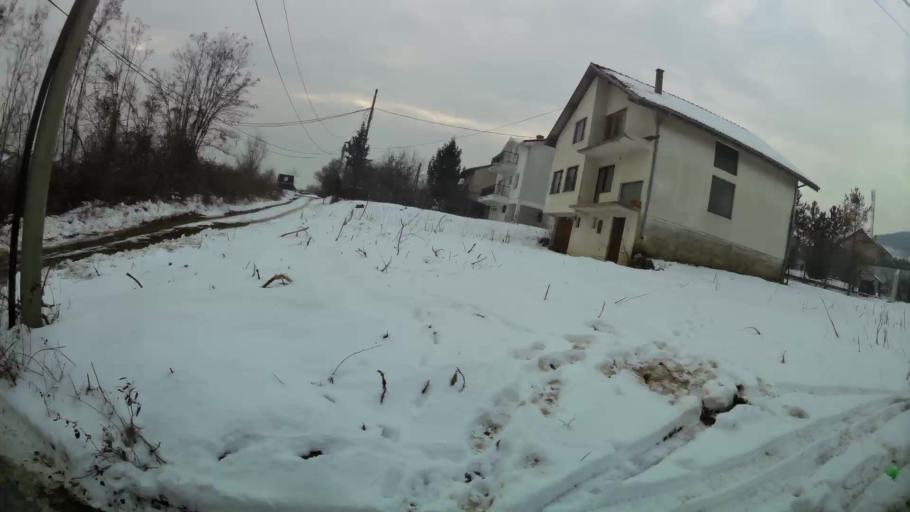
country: MK
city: Kondovo
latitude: 42.0459
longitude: 21.3411
